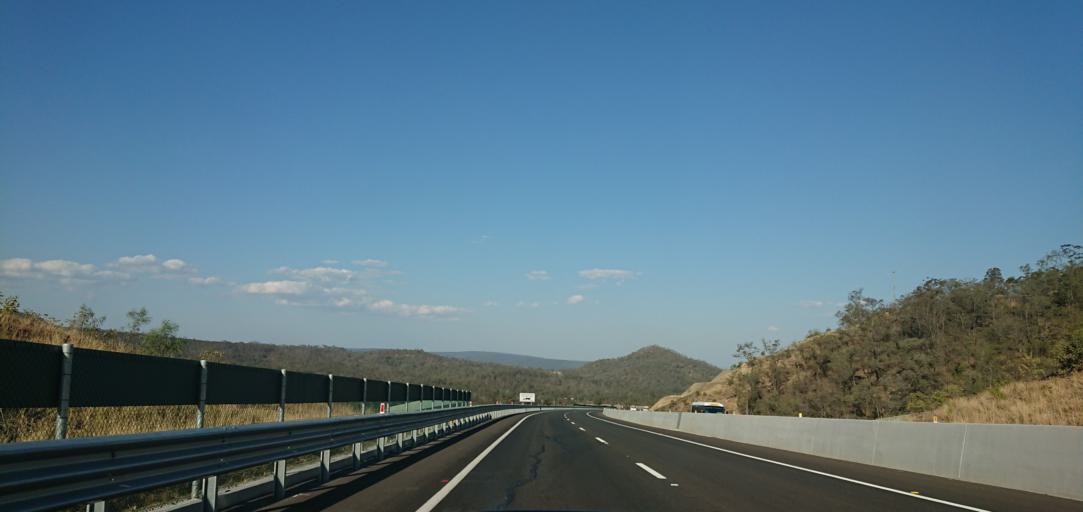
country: AU
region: Queensland
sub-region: Toowoomba
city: East Toowoomba
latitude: -27.5070
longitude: 152.0046
